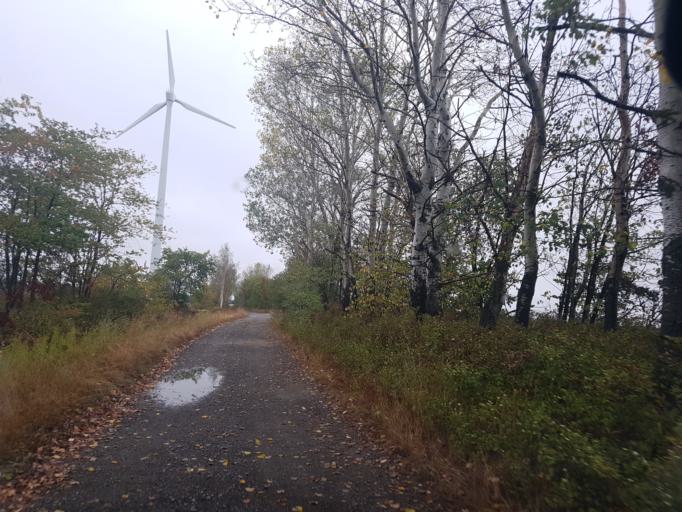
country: DE
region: Brandenburg
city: Merzdorf
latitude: 51.4212
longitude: 13.5079
